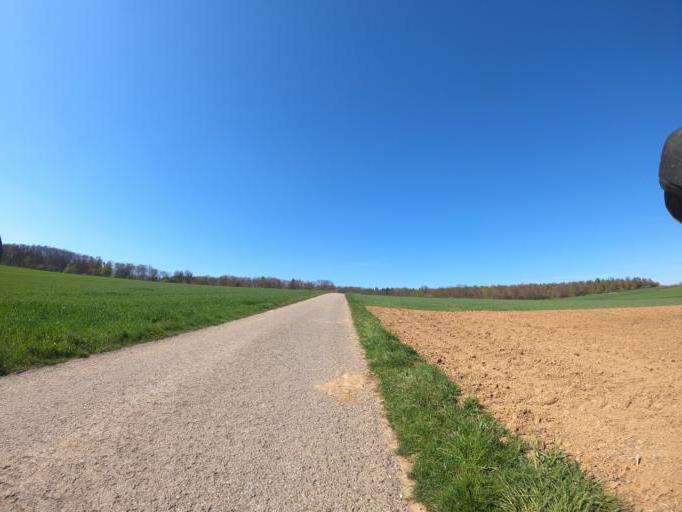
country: DE
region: Baden-Wuerttemberg
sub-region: Karlsruhe Region
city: Wiernsheim
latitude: 48.9142
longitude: 8.8755
